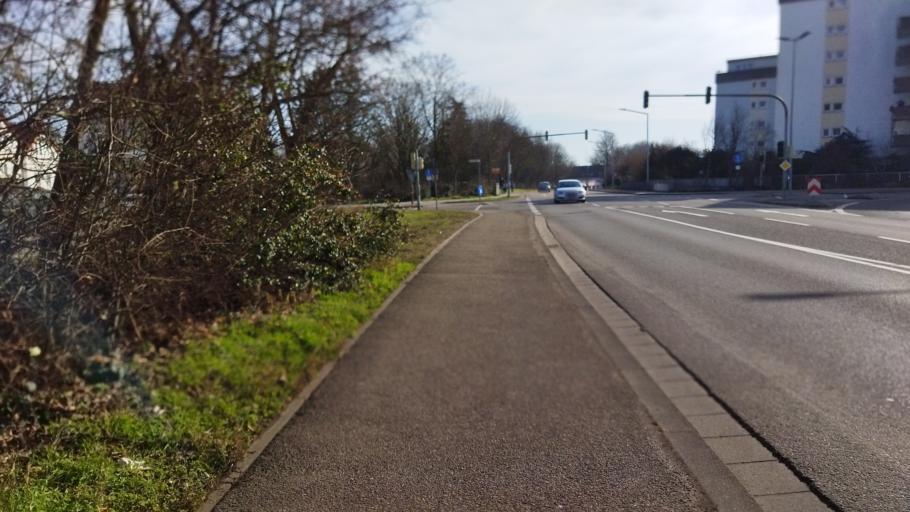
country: DE
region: Rheinland-Pfalz
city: Germersheim
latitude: 49.2087
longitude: 8.3644
